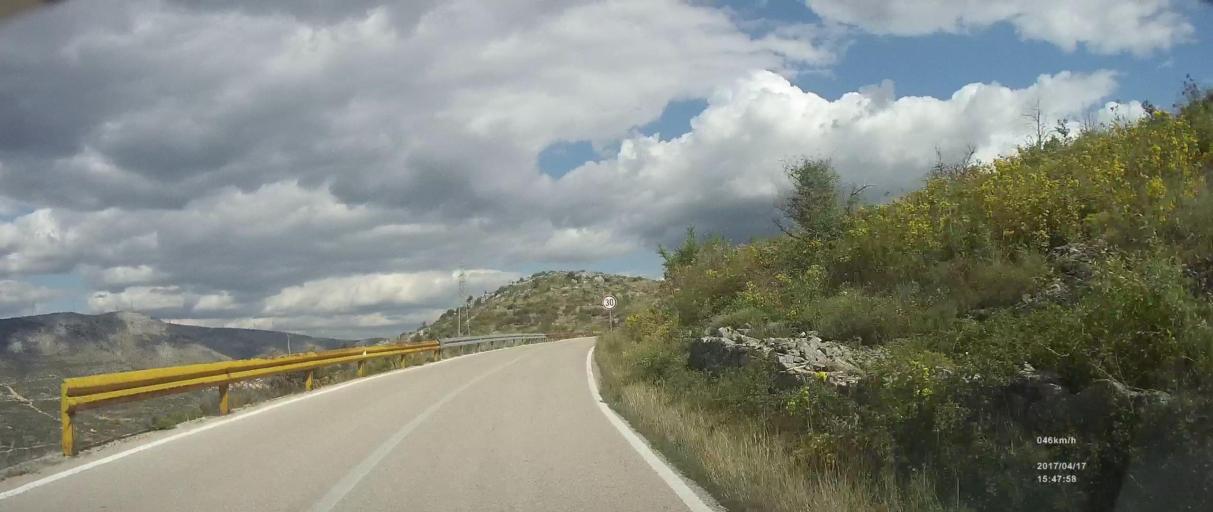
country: HR
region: Sibensko-Kniniska
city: Primosten
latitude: 43.6221
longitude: 15.9813
